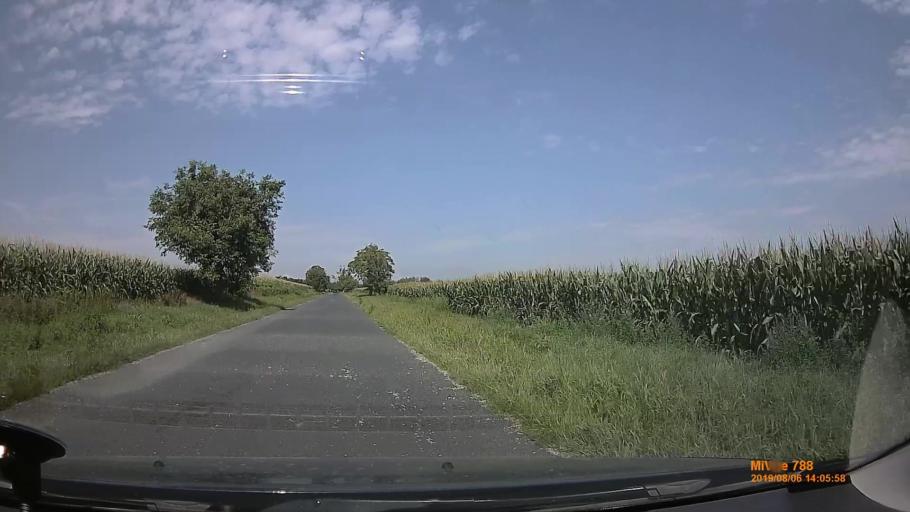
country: HU
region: Zala
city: Zalakomar
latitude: 46.5170
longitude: 17.0843
